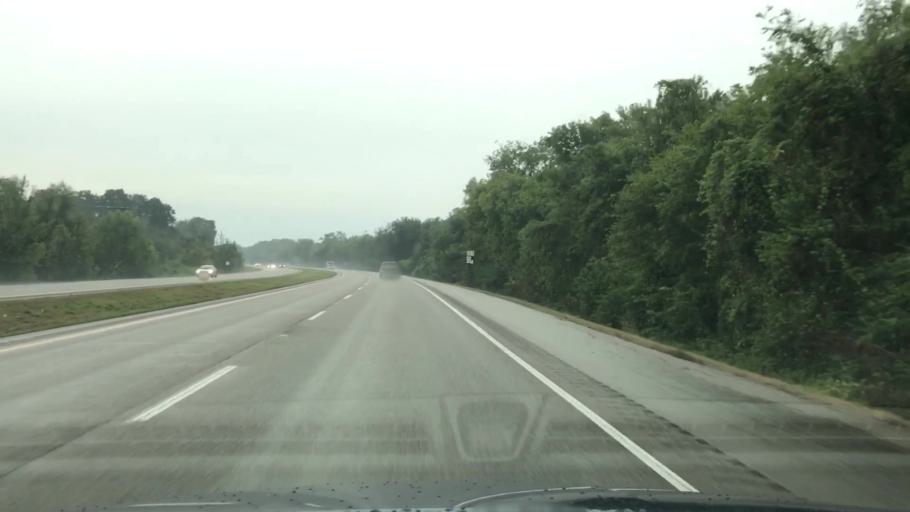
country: US
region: Louisiana
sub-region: Saint Charles Parish
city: Paradis
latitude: 29.8566
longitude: -90.4475
